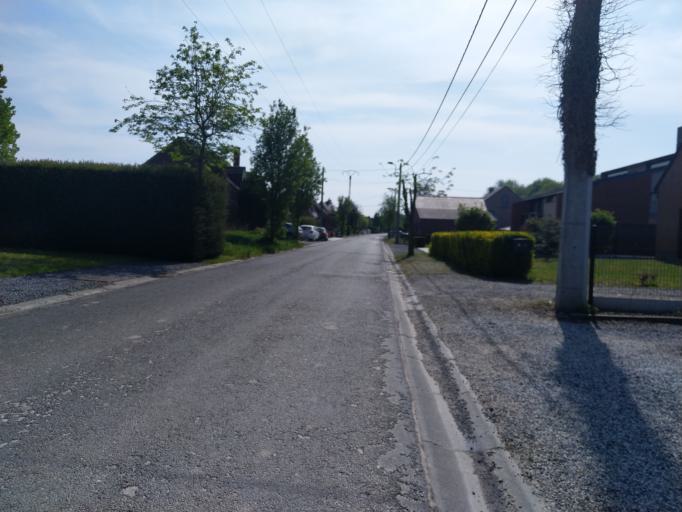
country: BE
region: Wallonia
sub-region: Province du Hainaut
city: Mons
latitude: 50.4416
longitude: 4.0217
